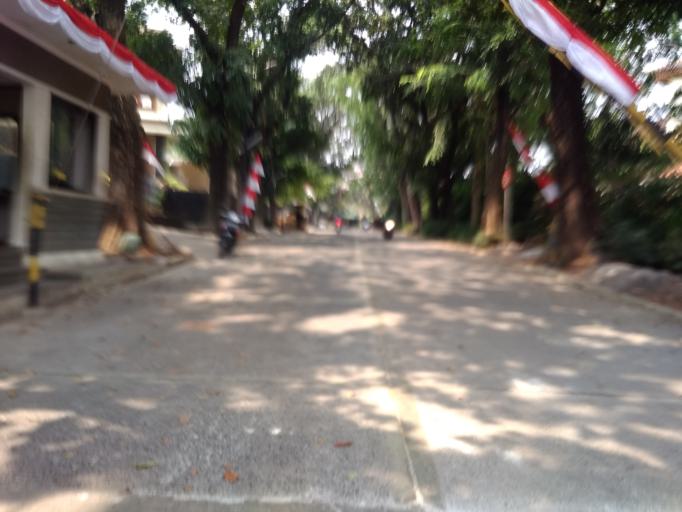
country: ID
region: West Java
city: Pamulang
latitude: -6.3191
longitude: 106.7890
